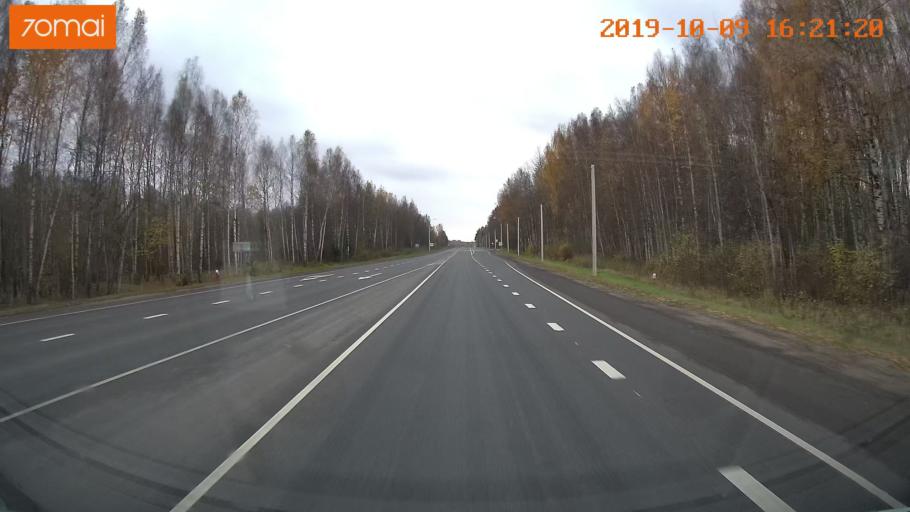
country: RU
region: Kostroma
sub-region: Kostromskoy Rayon
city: Kostroma
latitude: 57.6935
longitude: 40.8895
